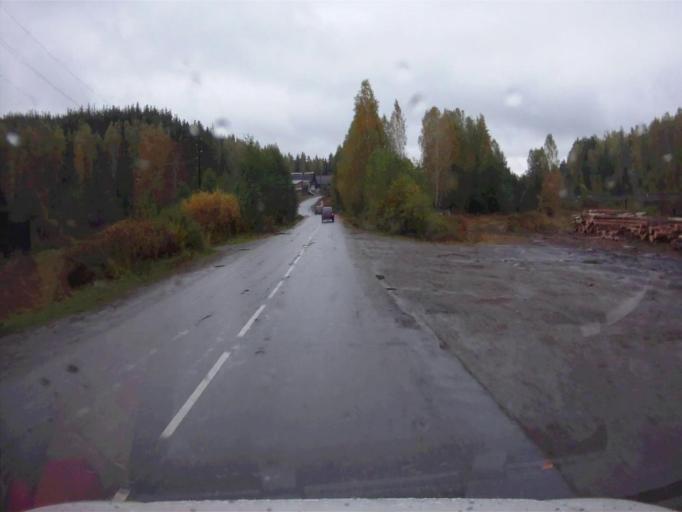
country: RU
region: Chelyabinsk
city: Kyshtym
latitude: 55.7634
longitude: 60.4859
